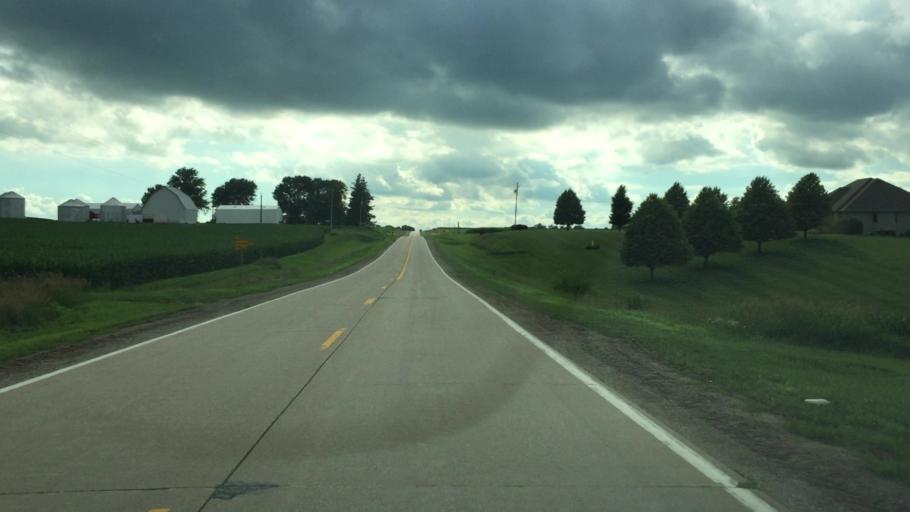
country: US
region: Iowa
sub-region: Jasper County
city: Monroe
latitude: 41.5808
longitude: -93.1157
